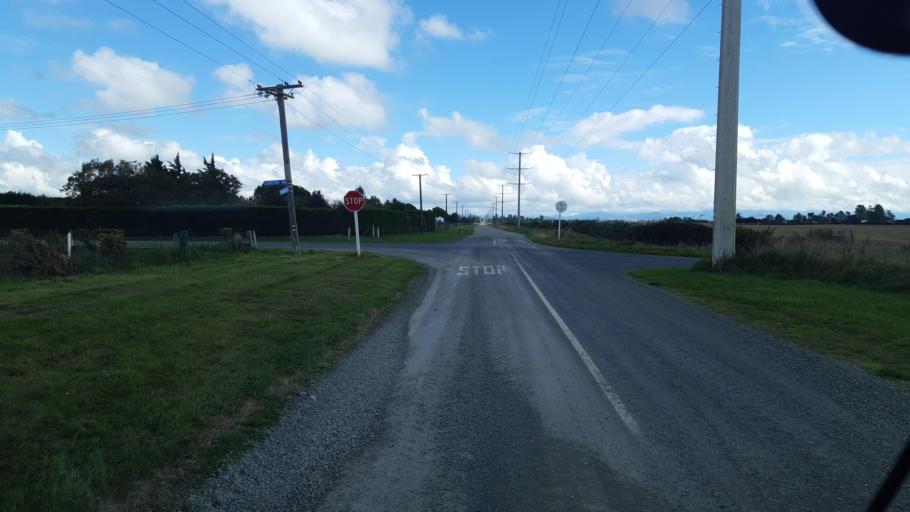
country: NZ
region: Canterbury
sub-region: Selwyn District
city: Darfield
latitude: -43.4728
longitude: 172.2257
